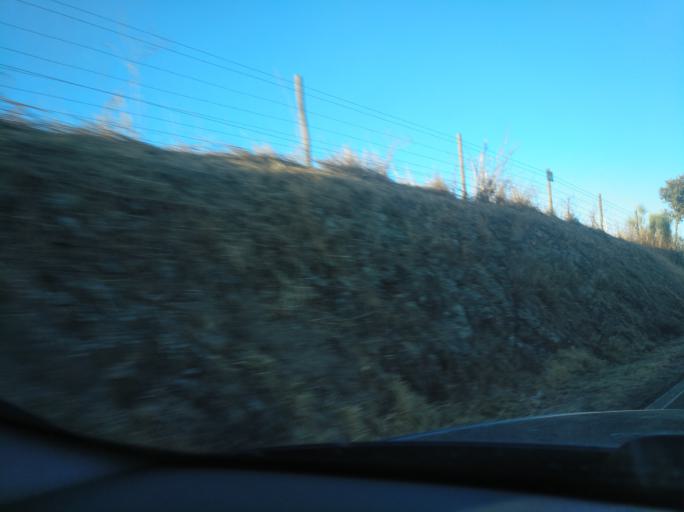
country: PT
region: Portalegre
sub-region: Arronches
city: Arronches
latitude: 39.0694
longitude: -7.2006
